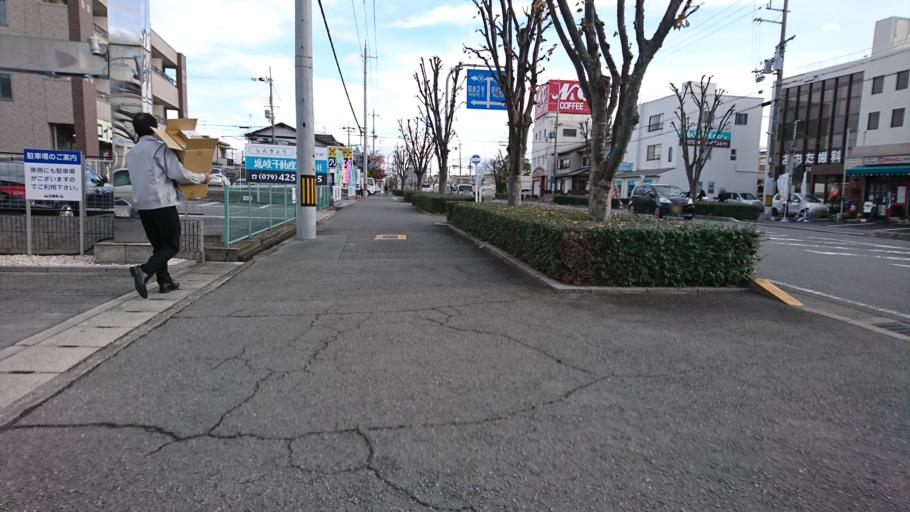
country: JP
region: Hyogo
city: Kakogawacho-honmachi
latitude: 34.7547
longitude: 134.8376
